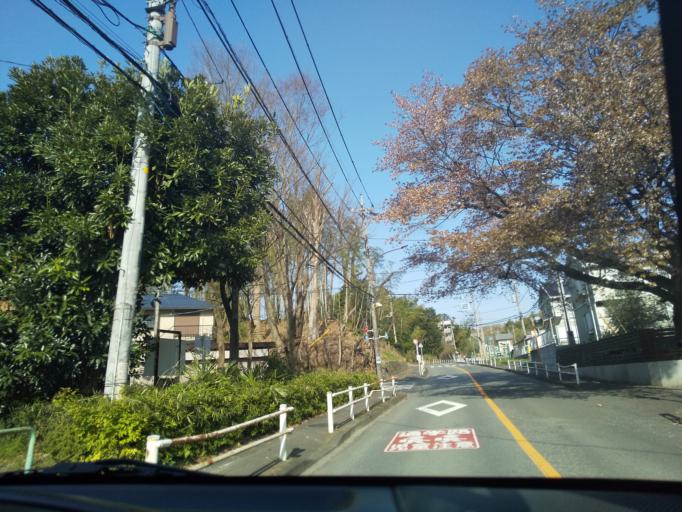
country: JP
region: Tokyo
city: Hino
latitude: 35.6430
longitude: 139.4270
